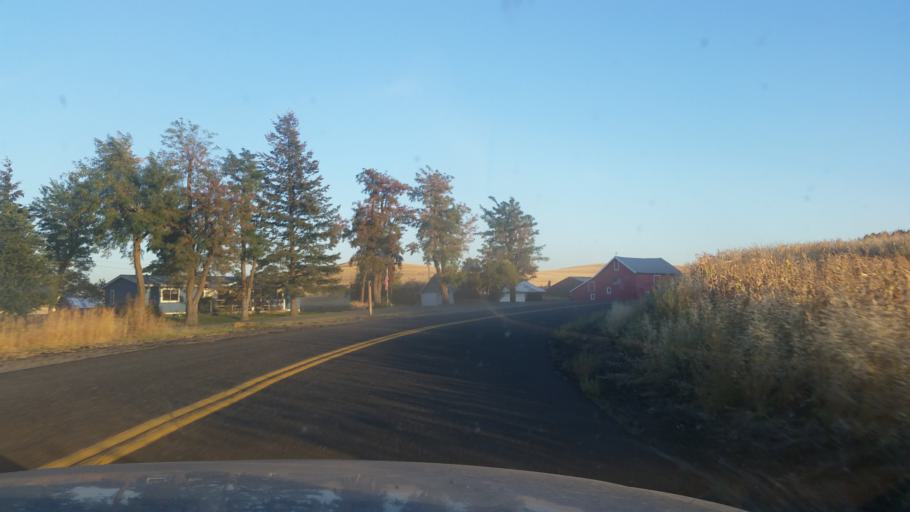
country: US
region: Washington
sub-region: Spokane County
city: Medical Lake
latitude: 47.5362
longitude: -117.6244
